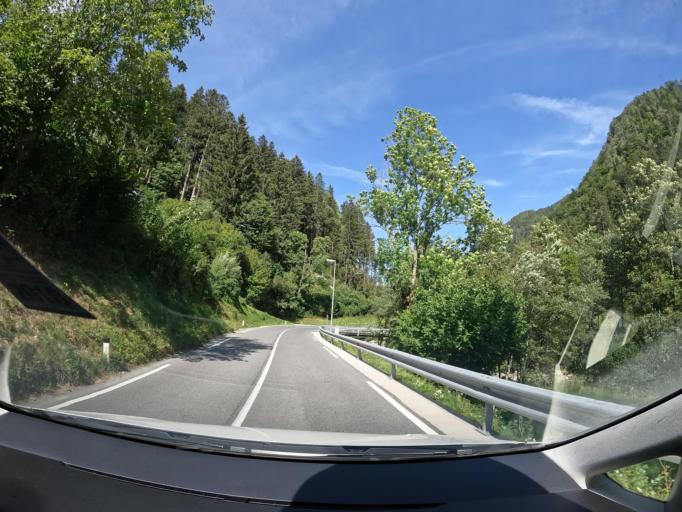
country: SI
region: Zirovnica
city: Zirovnica
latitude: 46.4414
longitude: 14.1885
